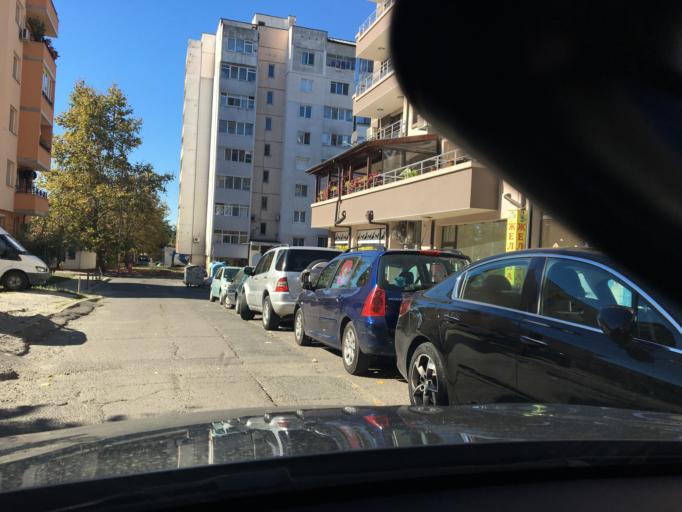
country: BG
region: Burgas
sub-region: Obshtina Burgas
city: Burgas
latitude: 42.5170
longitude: 27.4534
